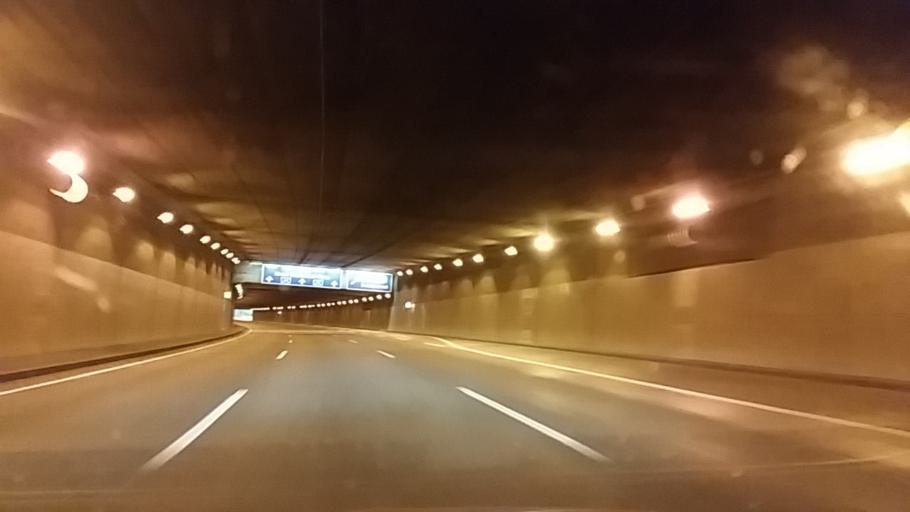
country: DE
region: North Rhine-Westphalia
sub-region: Regierungsbezirk Dusseldorf
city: Dusseldorf
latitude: 51.2737
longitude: 6.7684
